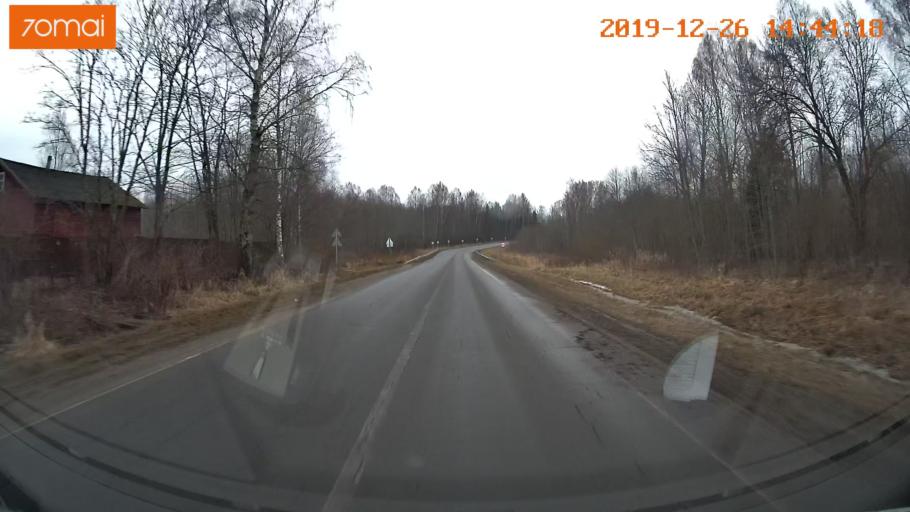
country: RU
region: Jaroslavl
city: Poshekhon'ye
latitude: 58.3495
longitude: 39.0491
